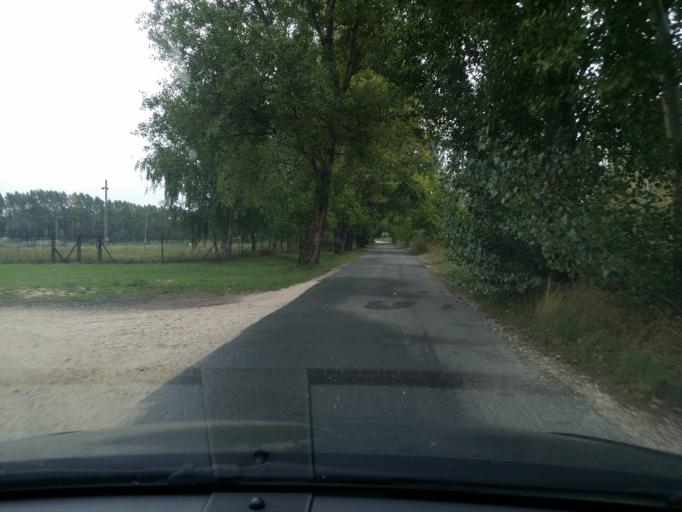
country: HU
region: Pest
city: Szigetcsep
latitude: 47.2309
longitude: 18.9640
